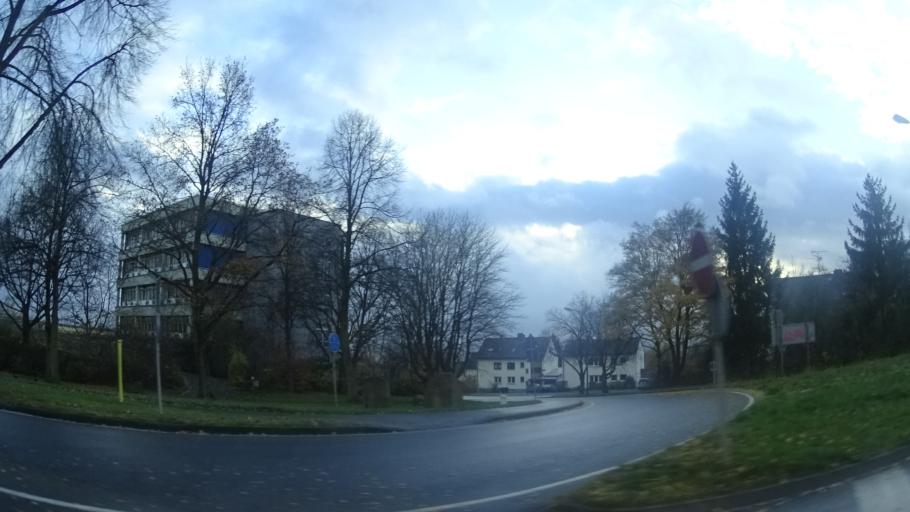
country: DE
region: Hesse
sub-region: Regierungsbezirk Kassel
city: Petersberg
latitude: 50.5583
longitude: 9.6945
